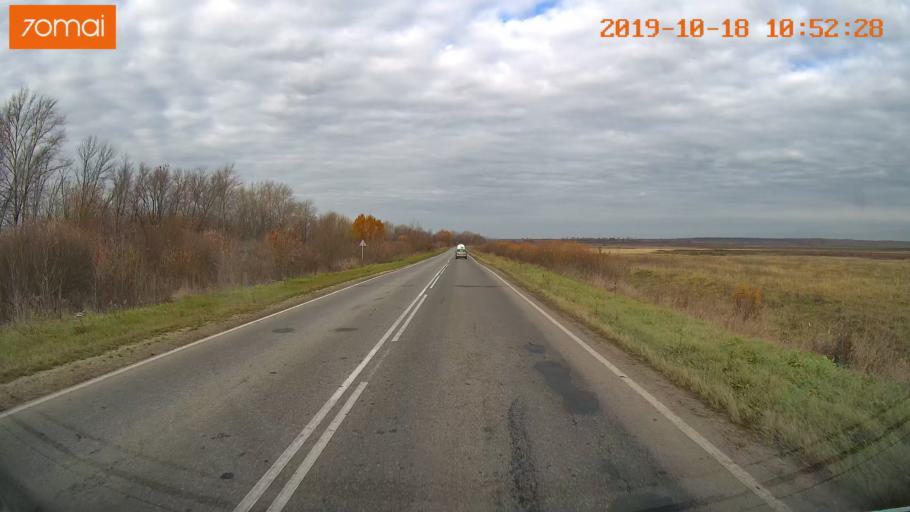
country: RU
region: Tula
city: Yepifan'
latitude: 53.7671
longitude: 38.6509
